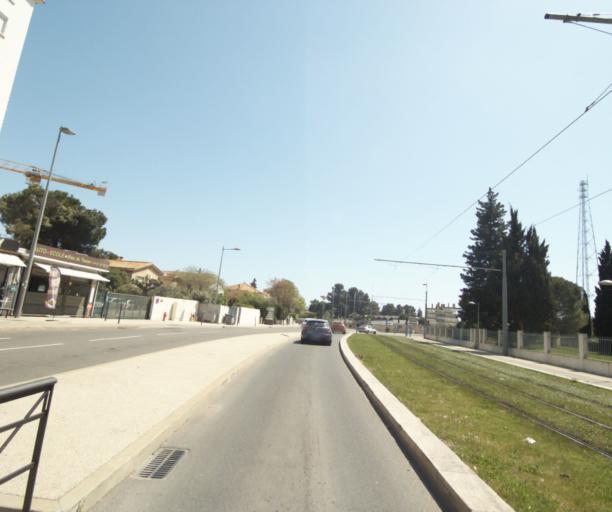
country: FR
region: Languedoc-Roussillon
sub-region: Departement de l'Herault
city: Montpellier
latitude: 43.6122
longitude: 3.8457
